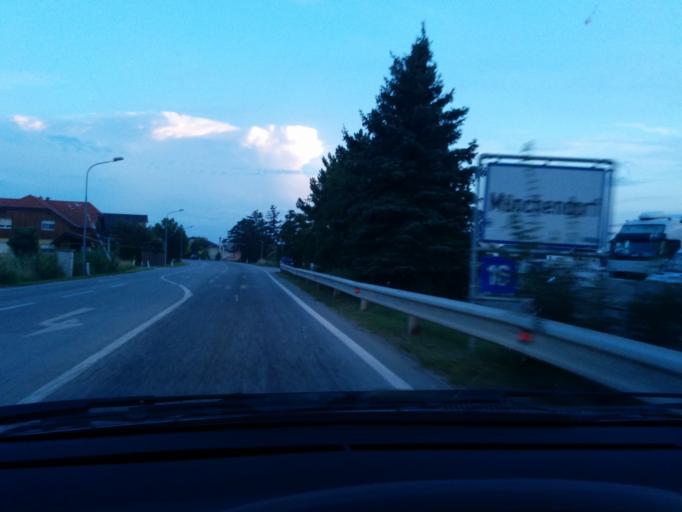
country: AT
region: Lower Austria
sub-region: Politischer Bezirk Modling
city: Munchendorf
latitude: 48.0375
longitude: 16.3796
